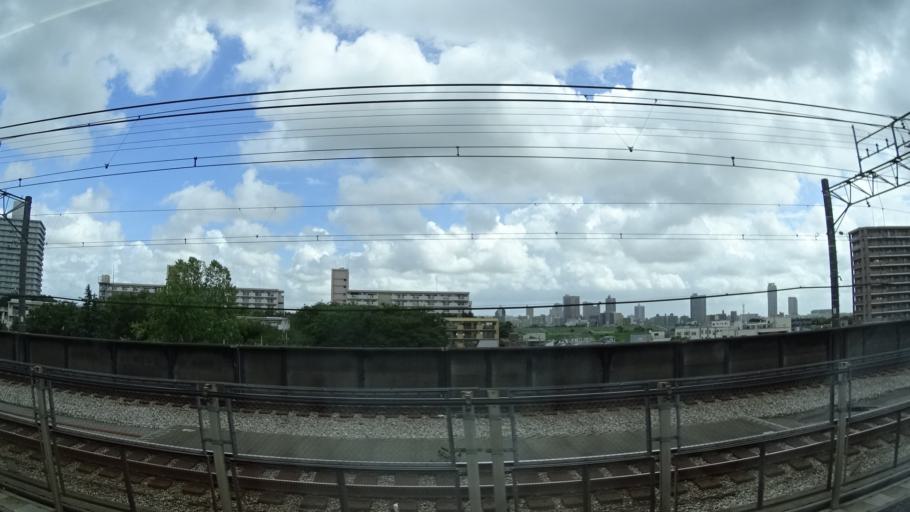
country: JP
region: Saitama
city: Kawaguchi
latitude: 35.7903
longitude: 139.6982
